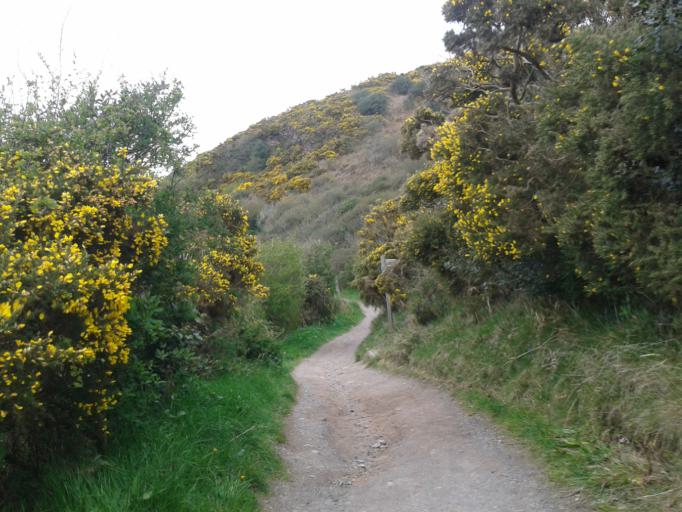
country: GB
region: England
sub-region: Devon
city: Braunton
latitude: 51.1511
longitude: -4.2122
